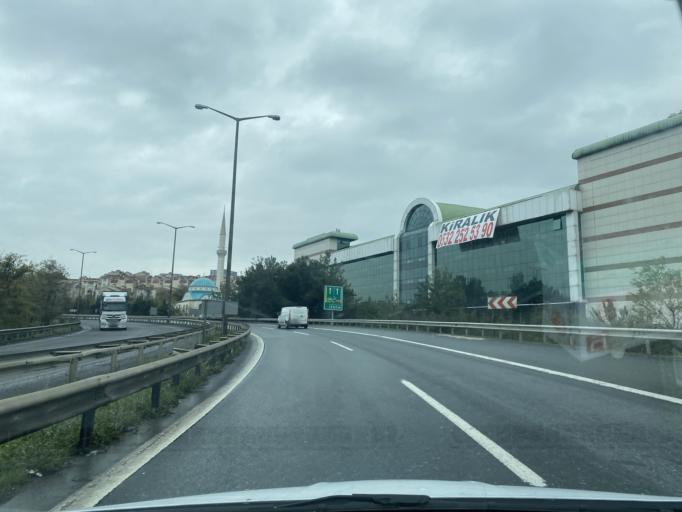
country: TR
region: Istanbul
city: Esenyurt
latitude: 41.0571
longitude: 28.6842
